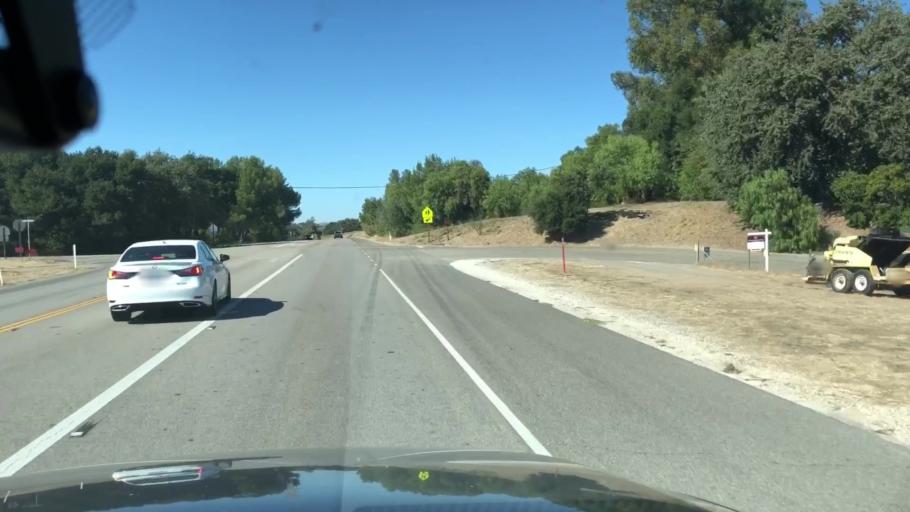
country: US
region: California
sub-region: Santa Barbara County
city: Los Olivos
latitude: 34.6654
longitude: -120.1099
